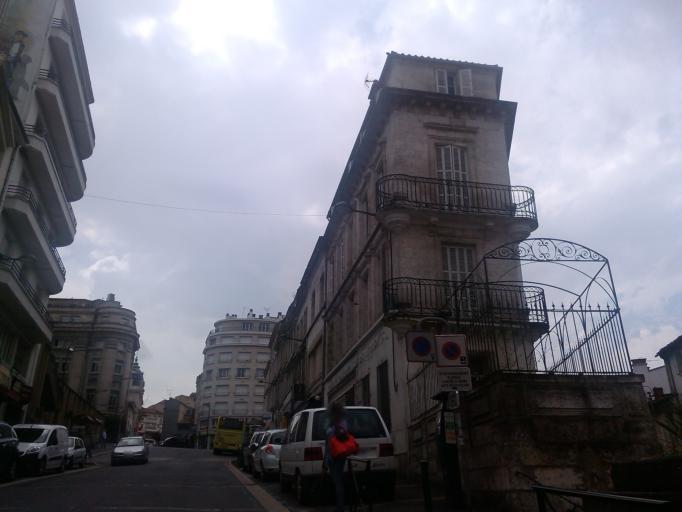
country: FR
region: Poitou-Charentes
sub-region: Departement de la Charente
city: Angouleme
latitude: 45.6499
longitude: 0.1603
